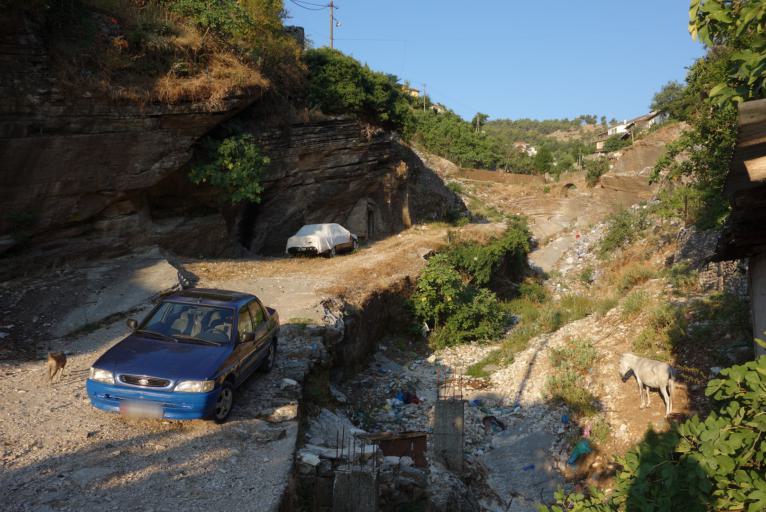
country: AL
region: Gjirokaster
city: Gjirokaster
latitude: 40.0702
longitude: 20.1353
